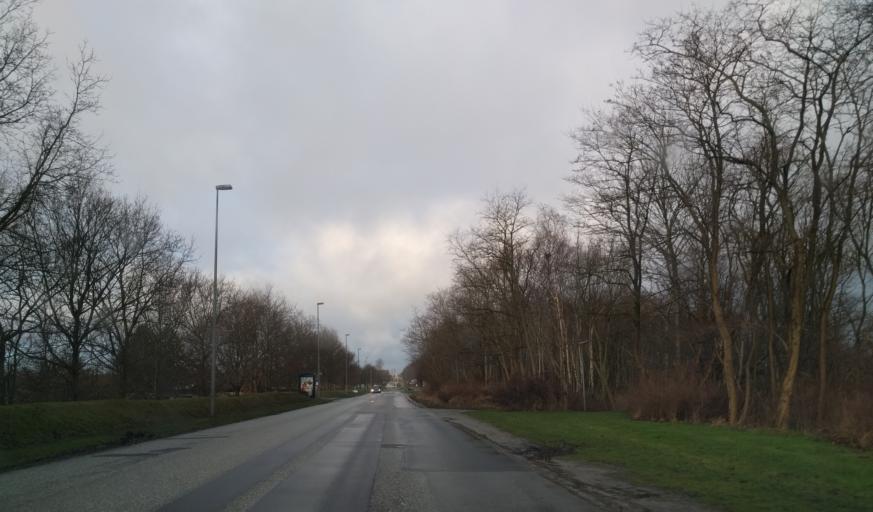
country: DK
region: North Denmark
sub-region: Alborg Kommune
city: Gistrup
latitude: 57.0184
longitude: 9.9809
